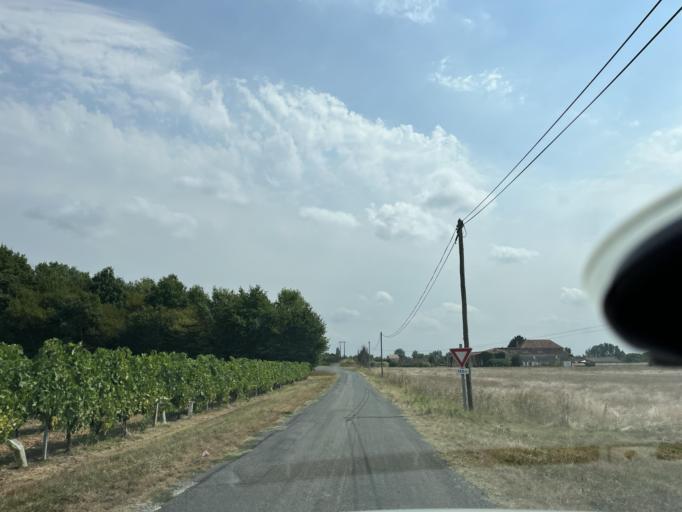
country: FR
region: Poitou-Charentes
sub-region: Departement de la Charente-Maritime
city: Pons
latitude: 45.6052
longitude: -0.5963
